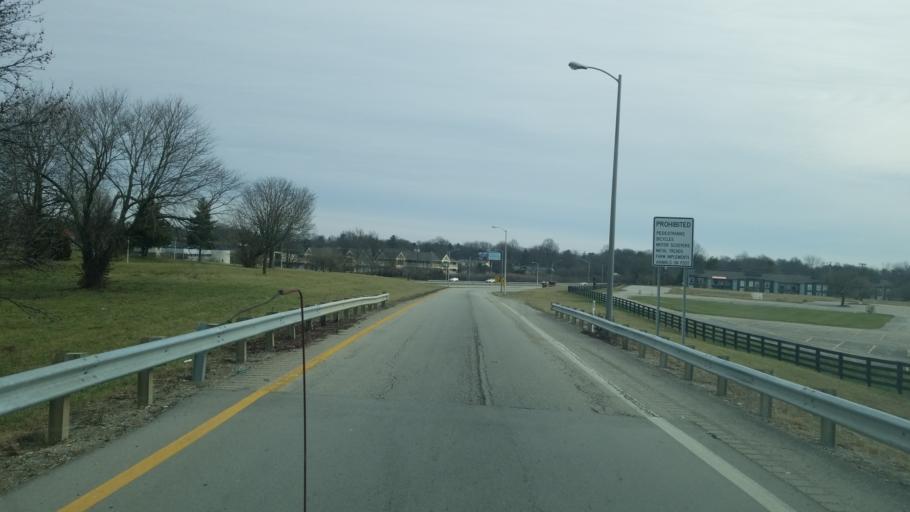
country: US
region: Kentucky
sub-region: Fayette County
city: Monticello
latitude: 37.9951
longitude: -84.5214
